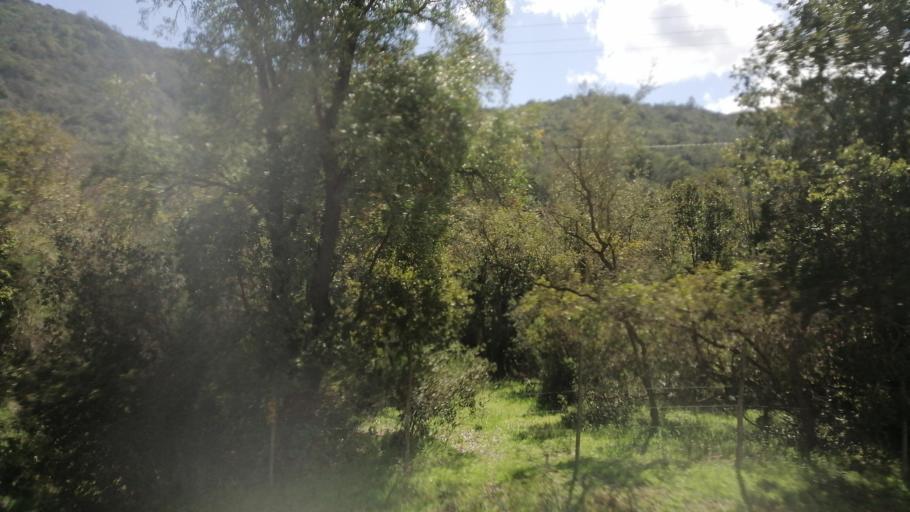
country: CL
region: Valparaiso
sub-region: Provincia de Marga Marga
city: Limache
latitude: -33.1992
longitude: -71.2363
